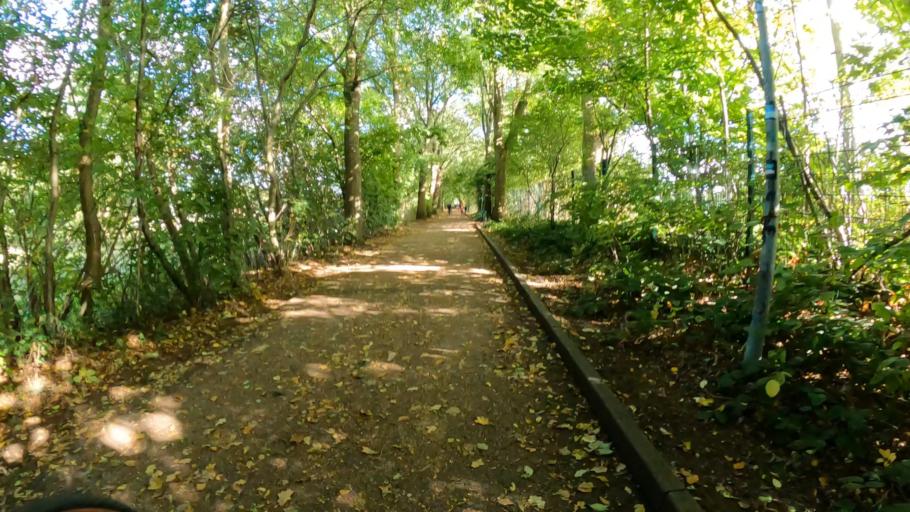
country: DE
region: Schleswig-Holstein
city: Henstedt-Ulzburg
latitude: 53.7922
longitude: 9.9914
